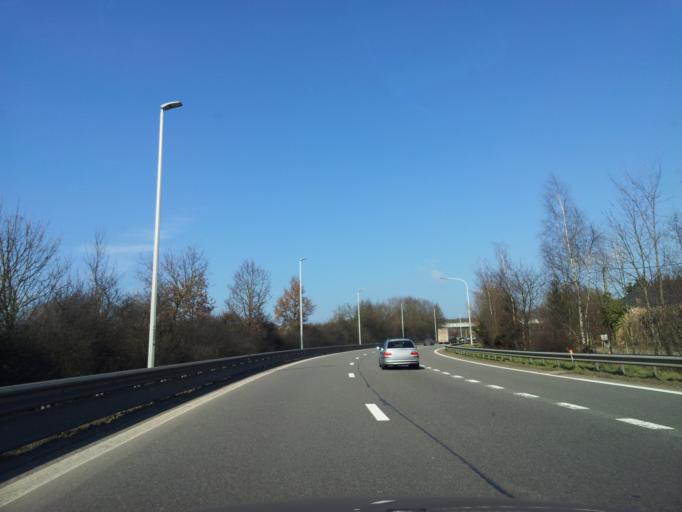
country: BE
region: Wallonia
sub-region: Province de Liege
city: Dison
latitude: 50.6329
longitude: 5.8385
